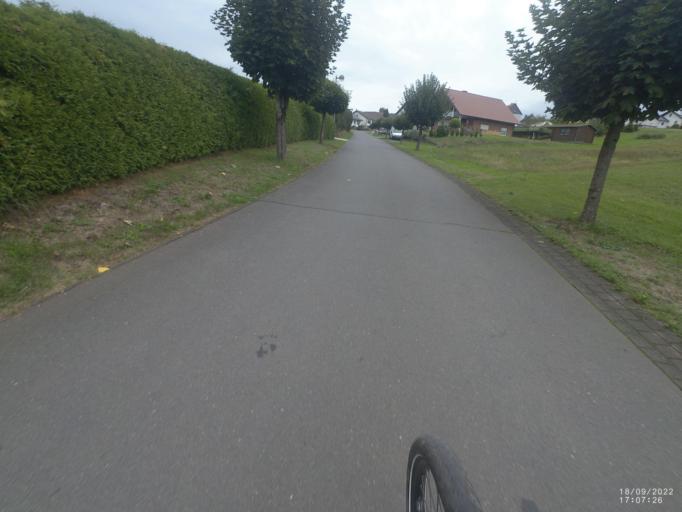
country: DE
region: Rheinland-Pfalz
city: Weidenbach
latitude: 50.1271
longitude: 6.7075
